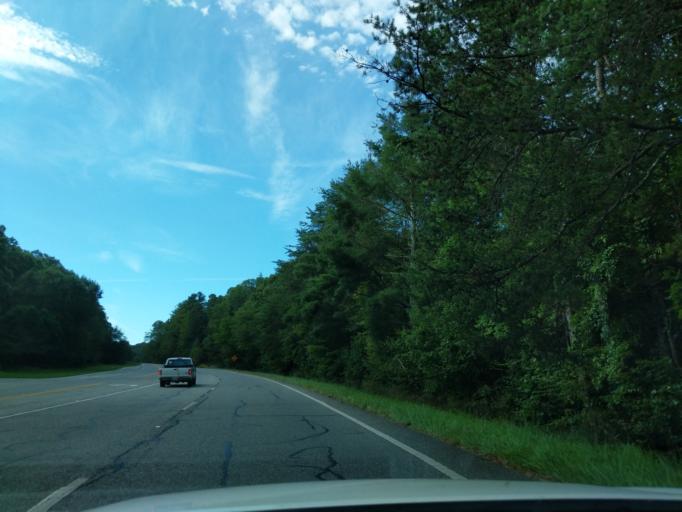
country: US
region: Georgia
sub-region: Fannin County
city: McCaysville
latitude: 34.9389
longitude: -84.3762
